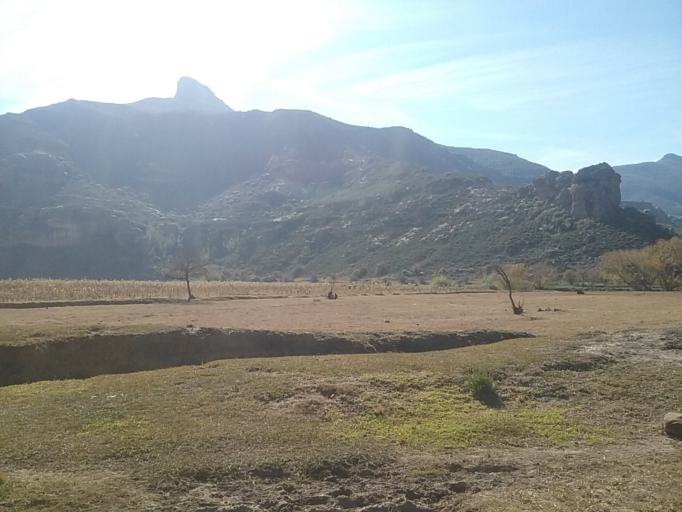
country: LS
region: Berea
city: Teyateyaneng
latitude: -29.2519
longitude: 27.9201
